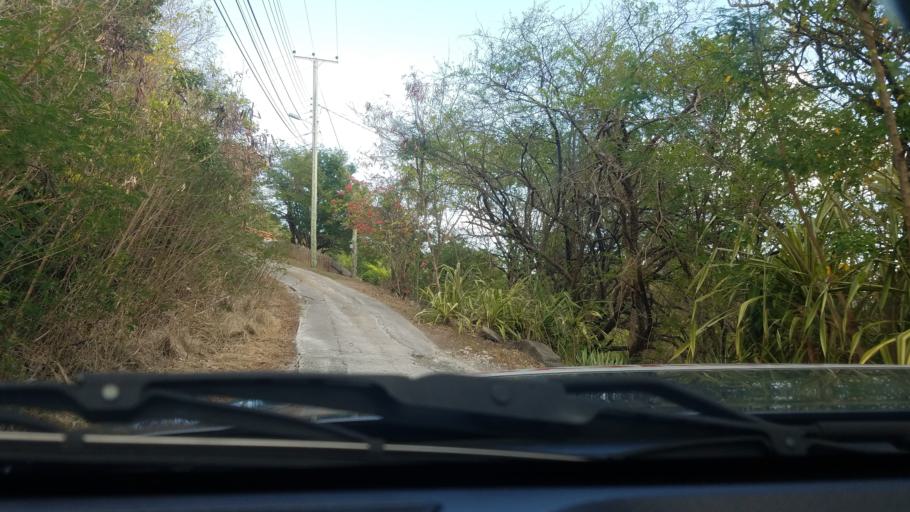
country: LC
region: Gros-Islet
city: Gros Islet
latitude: 14.1048
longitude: -60.9448
